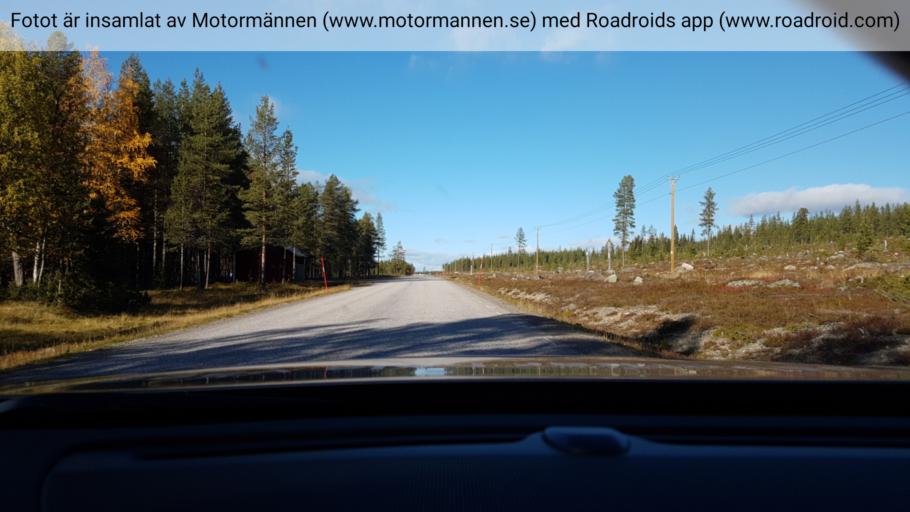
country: SE
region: Vaesterbotten
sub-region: Mala Kommun
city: Mala
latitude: 65.7711
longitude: 18.5337
